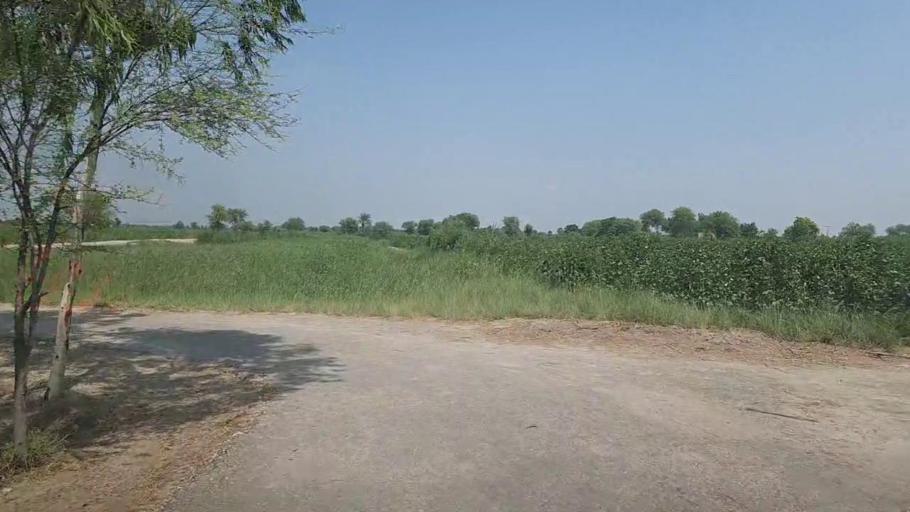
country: PK
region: Sindh
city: Ubauro
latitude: 28.1562
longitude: 69.8178
